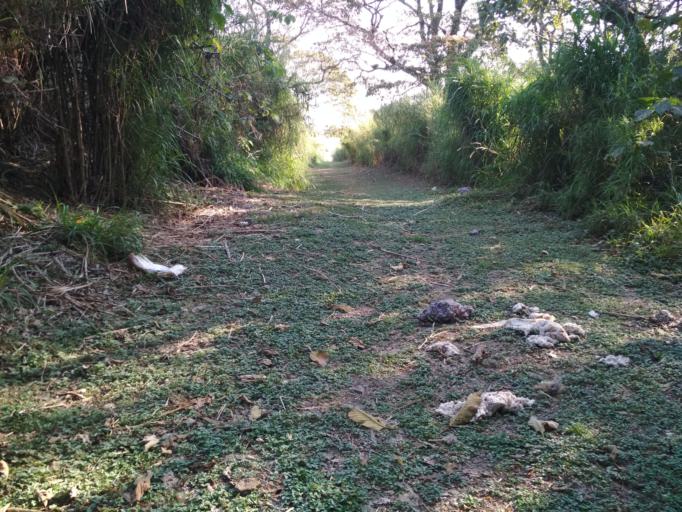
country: MX
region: Veracruz
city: Ixtac Zoquitlan
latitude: 18.8624
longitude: -97.0710
